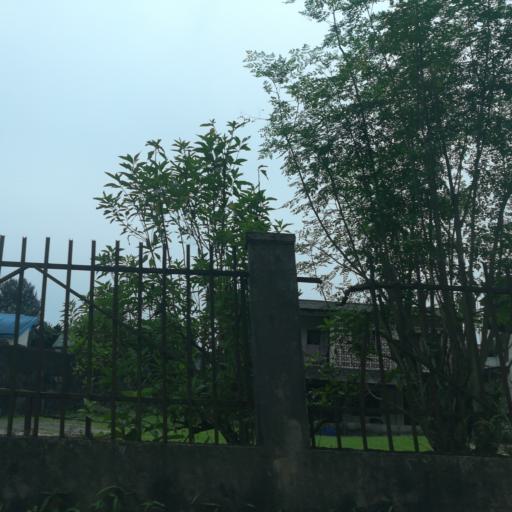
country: NG
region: Rivers
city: Port Harcourt
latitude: 4.7950
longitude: 7.0075
